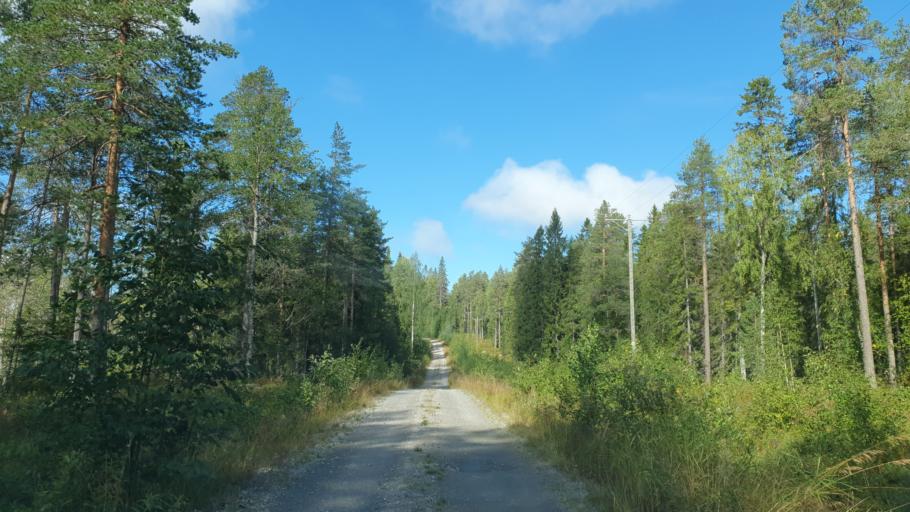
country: FI
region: Kainuu
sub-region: Kehys-Kainuu
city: Kuhmo
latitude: 64.0388
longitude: 29.1395
